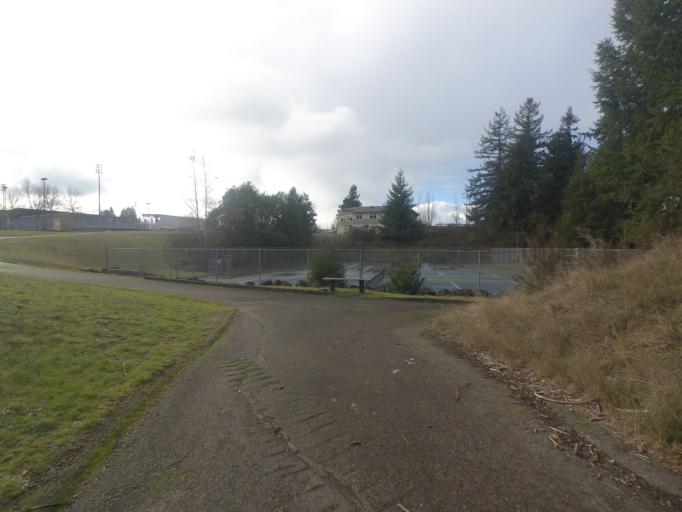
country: US
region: Washington
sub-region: Pierce County
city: University Place
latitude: 47.2243
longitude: -122.5503
